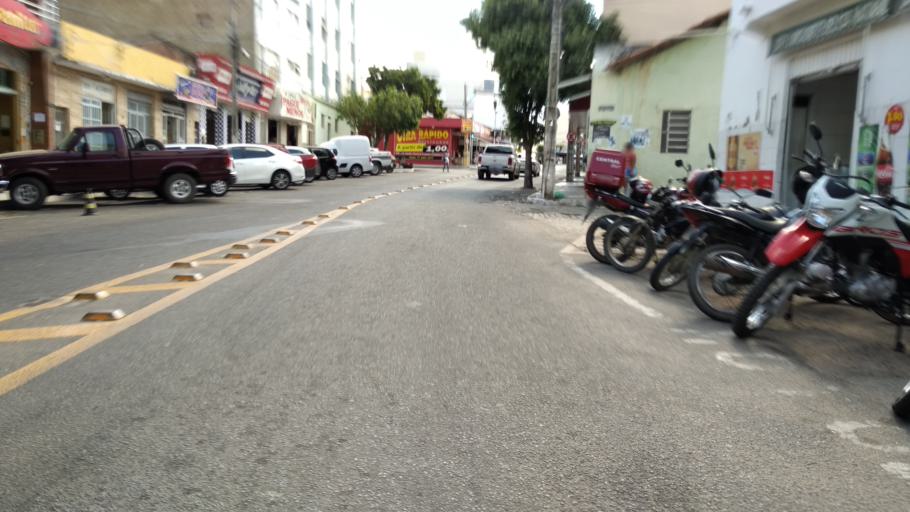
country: BR
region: Bahia
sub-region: Guanambi
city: Guanambi
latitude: -14.2289
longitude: -42.7803
